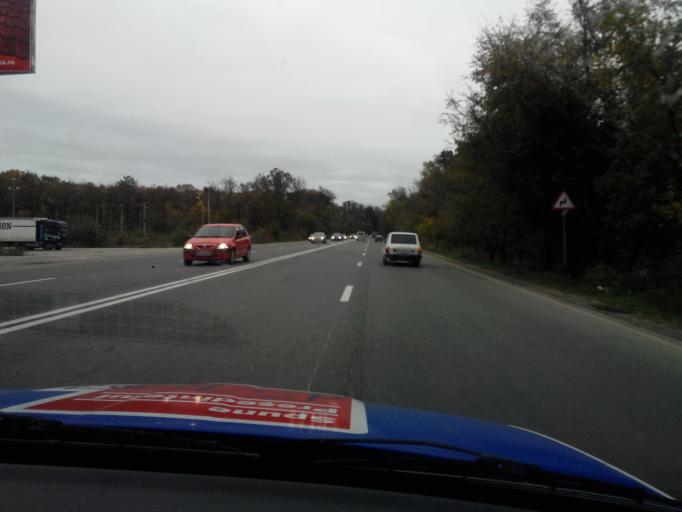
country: RO
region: Ilfov
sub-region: Comuna Jilava
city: Jilava
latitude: 44.3144
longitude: 26.0651
